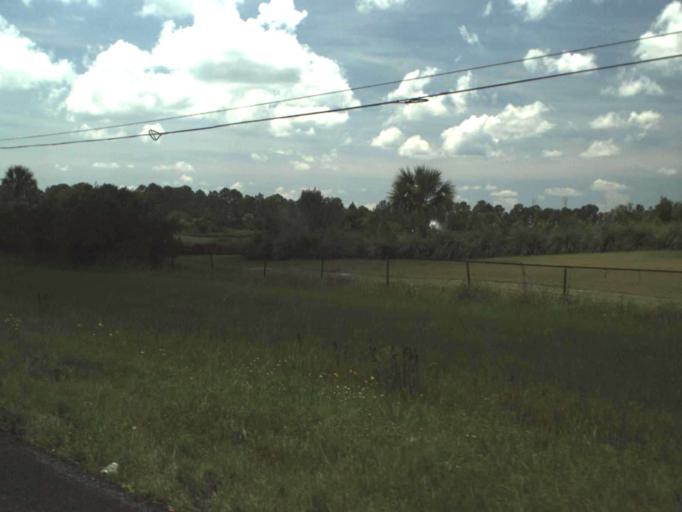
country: US
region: Florida
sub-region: Volusia County
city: Glencoe
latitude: 29.0122
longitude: -81.0193
